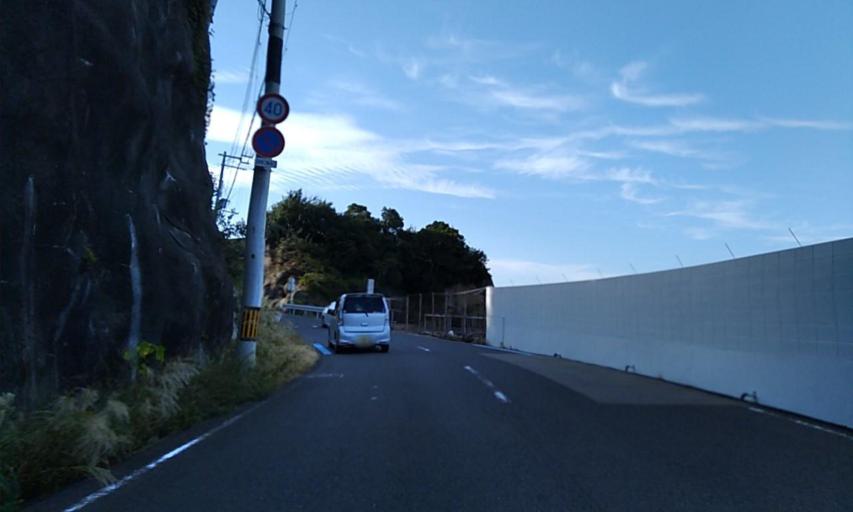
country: JP
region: Wakayama
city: Tanabe
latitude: 33.6934
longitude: 135.3417
